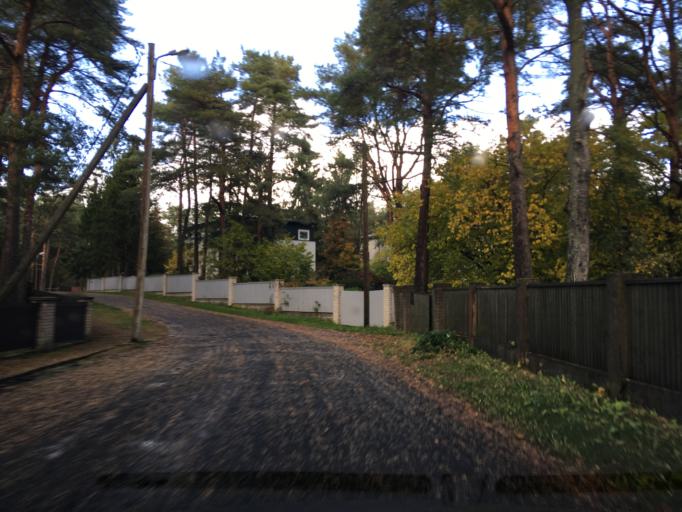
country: EE
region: Harju
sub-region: Tallinna linn
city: Tallinn
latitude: 59.3804
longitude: 24.7119
